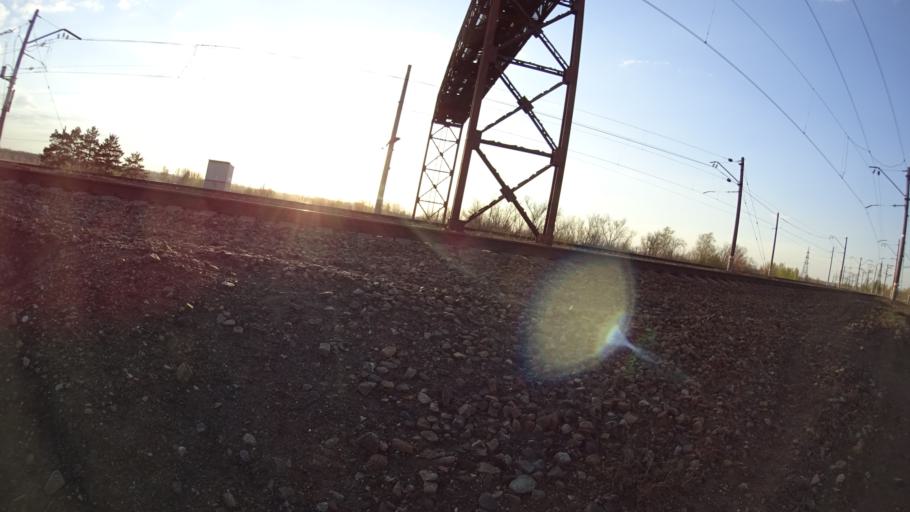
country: RU
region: Chelyabinsk
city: Troitsk
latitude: 54.0580
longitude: 61.6137
